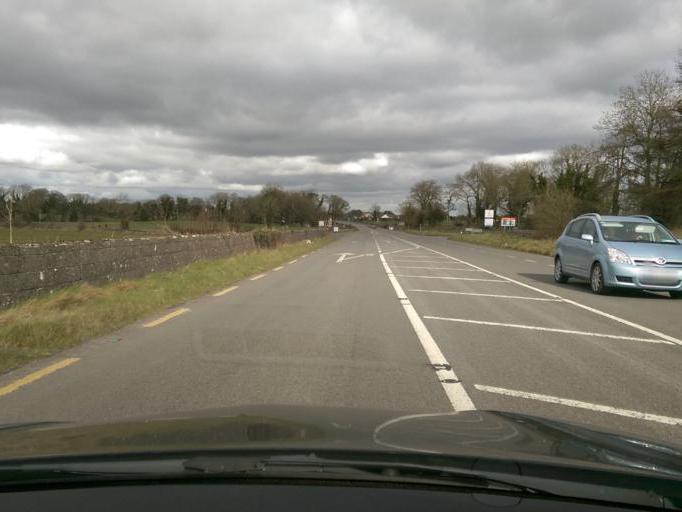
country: IE
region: Connaught
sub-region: County Galway
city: Ballinasloe
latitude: 53.3447
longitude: -8.0949
